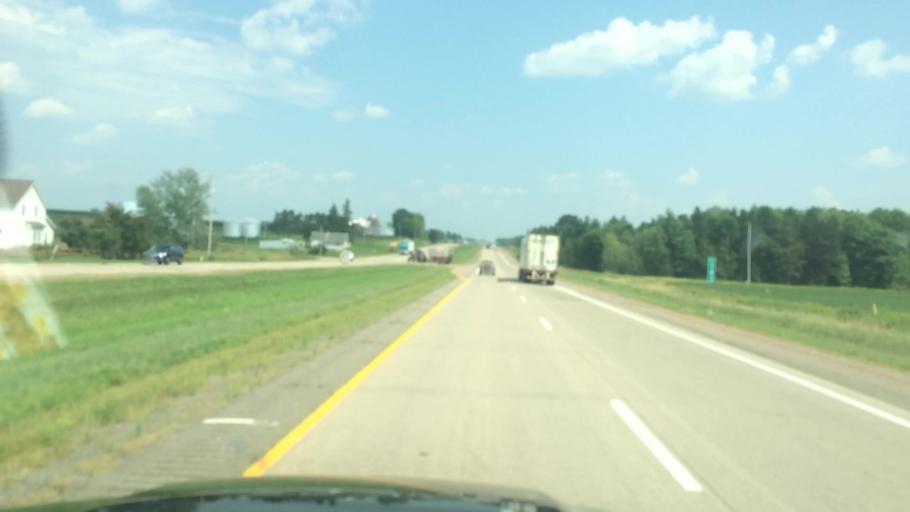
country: US
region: Wisconsin
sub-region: Marathon County
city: Athens
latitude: 44.9453
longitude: -90.1222
